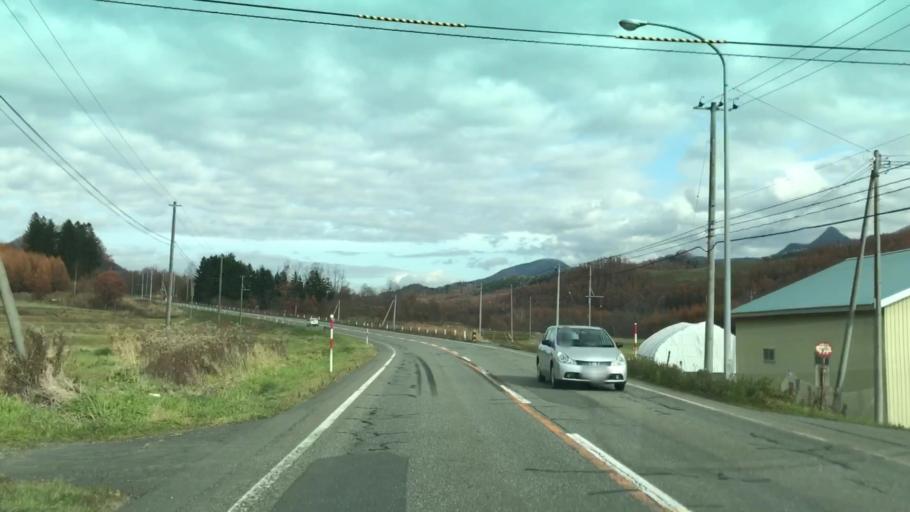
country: JP
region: Hokkaido
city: Shizunai-furukawacho
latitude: 42.7417
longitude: 142.3617
